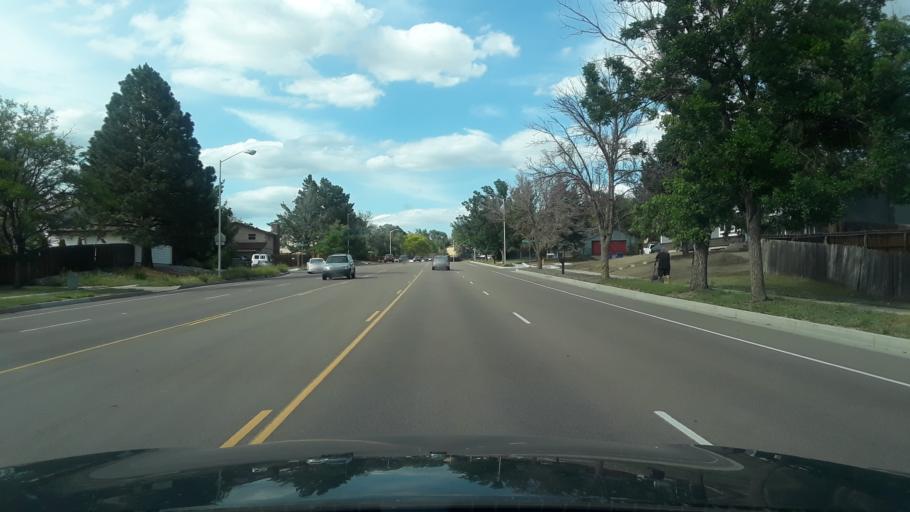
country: US
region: Colorado
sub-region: El Paso County
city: Cimarron Hills
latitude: 38.8837
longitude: -104.7507
